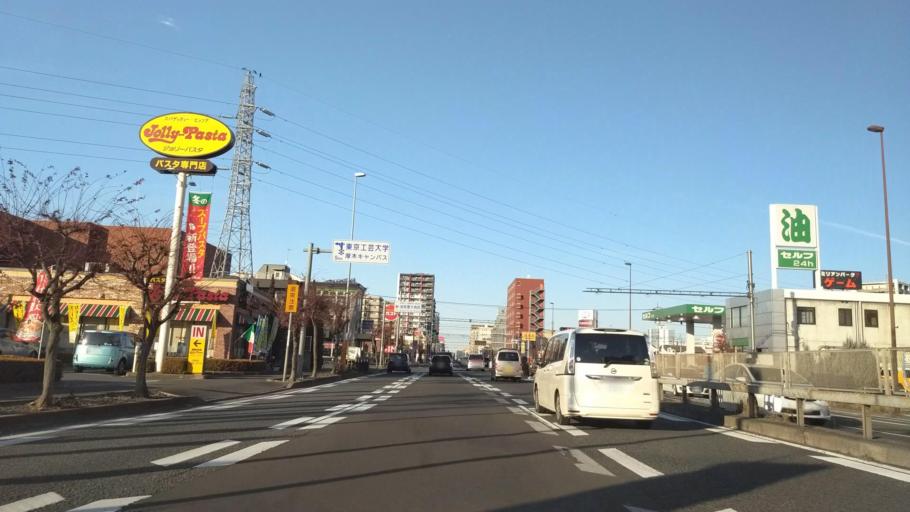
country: JP
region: Kanagawa
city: Atsugi
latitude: 35.4345
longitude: 139.3570
